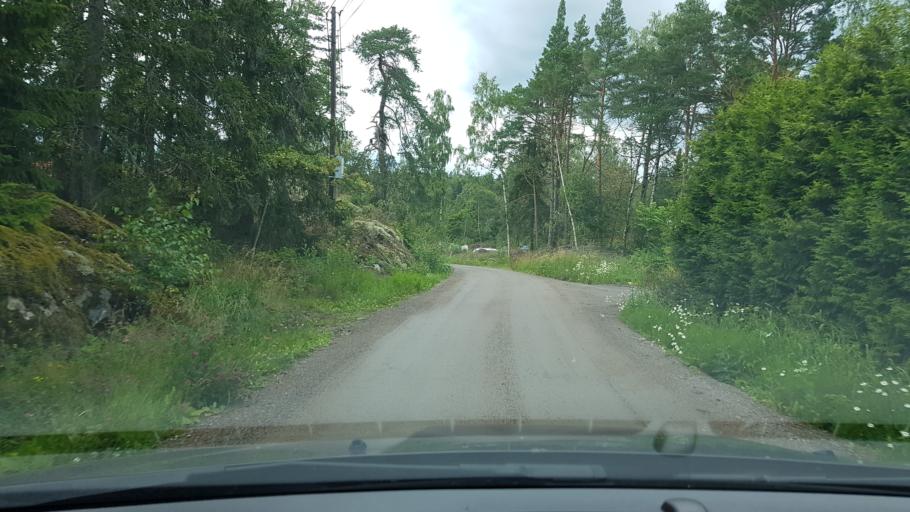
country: SE
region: Uppsala
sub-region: Uppsala Kommun
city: Alsike
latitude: 59.7165
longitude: 17.7020
